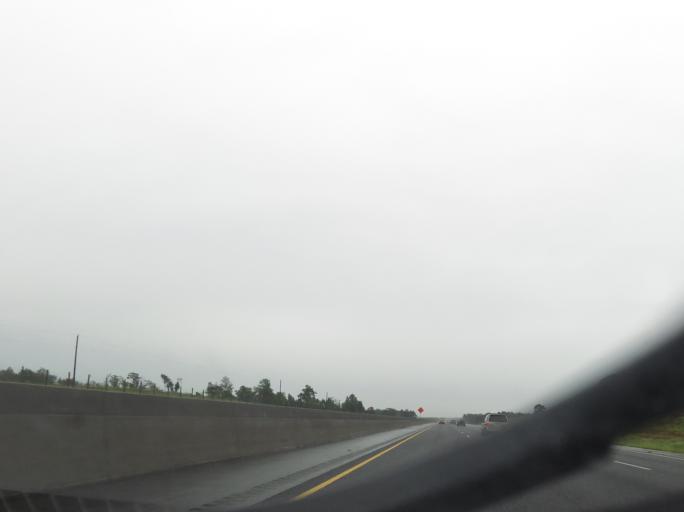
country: US
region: Georgia
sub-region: Tift County
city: Tifton
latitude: 31.5308
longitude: -83.5240
